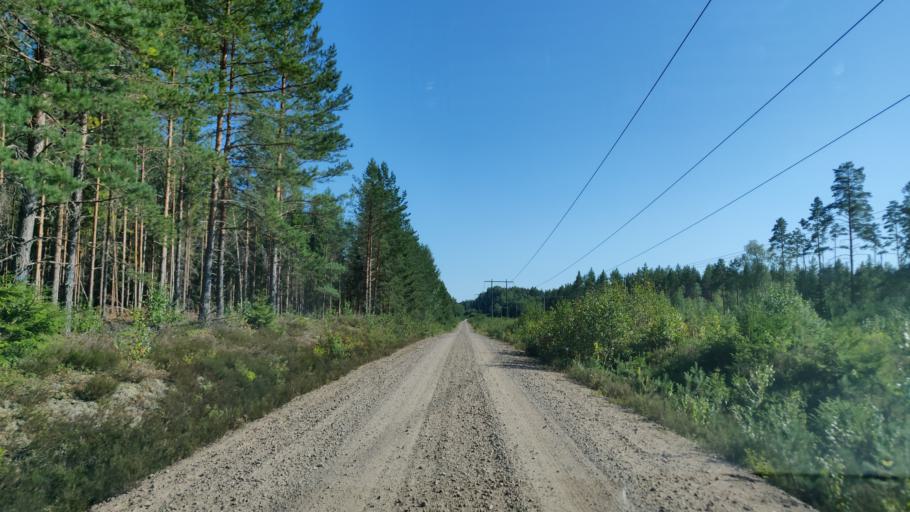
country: SE
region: Vaermland
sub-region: Hagfors Kommun
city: Ekshaerad
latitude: 60.0530
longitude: 13.5223
